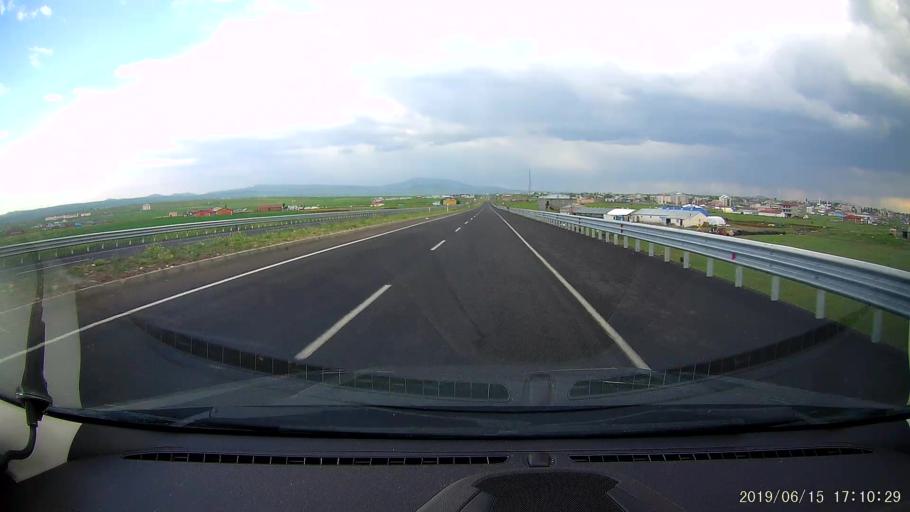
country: TR
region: Kars
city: Kars
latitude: 40.6218
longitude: 43.1337
